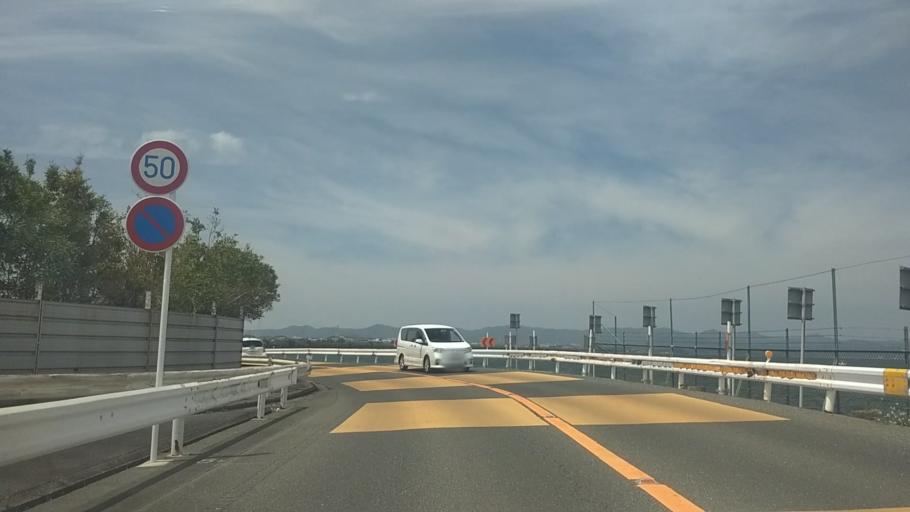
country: JP
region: Shizuoka
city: Kosai-shi
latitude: 34.7012
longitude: 137.5748
